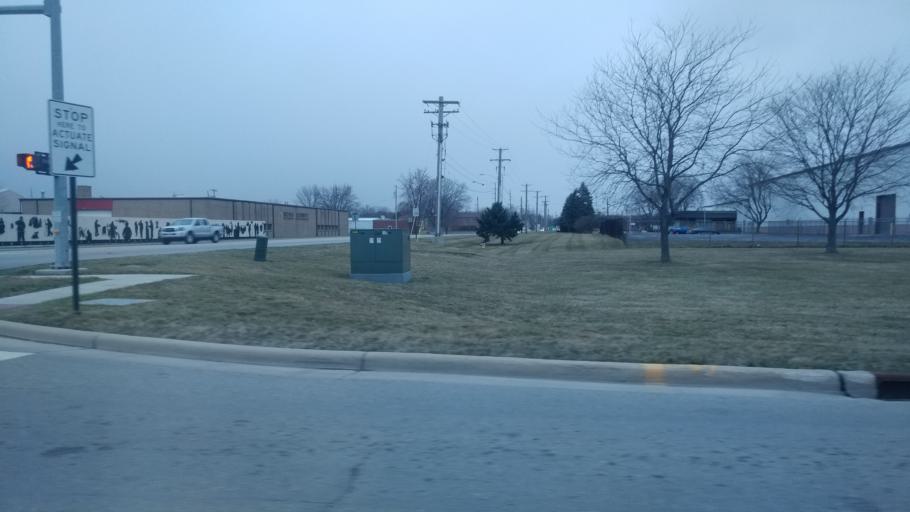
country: US
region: Ohio
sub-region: Wood County
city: Bowling Green
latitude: 41.3857
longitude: -83.6413
